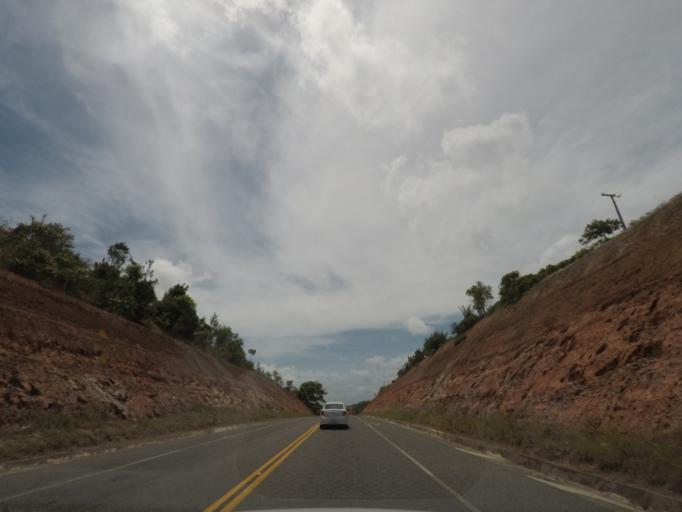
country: BR
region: Bahia
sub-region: Conde
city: Conde
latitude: -11.9115
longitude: -37.6582
